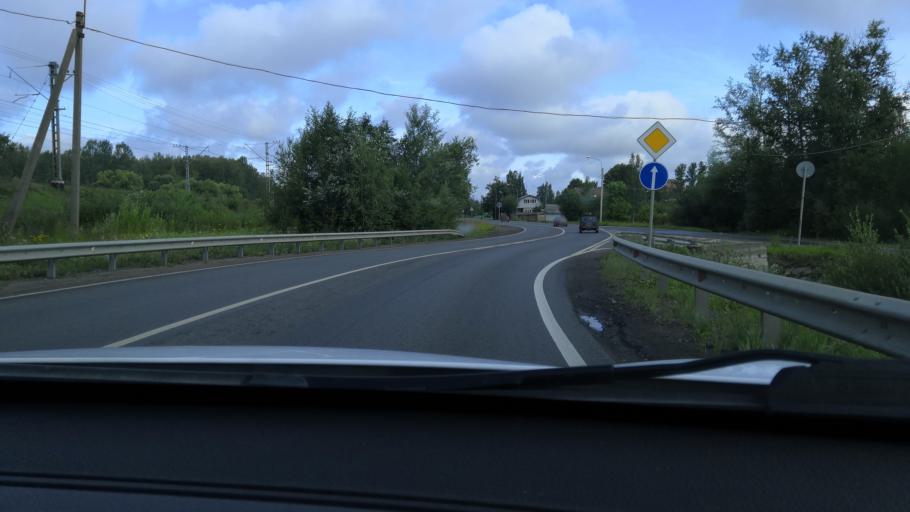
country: RU
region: St.-Petersburg
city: Tyarlevo
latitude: 59.7048
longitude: 30.4387
